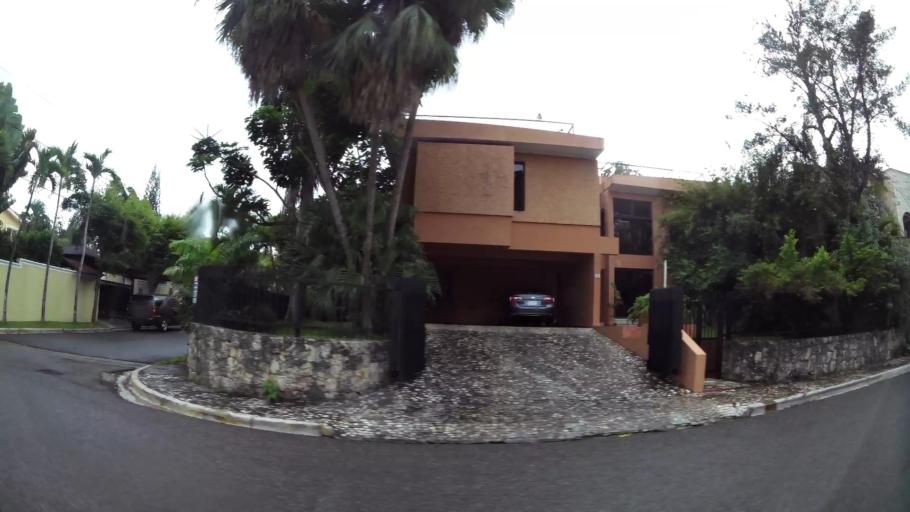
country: DO
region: Nacional
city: La Agustina
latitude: 18.5103
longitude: -69.9510
